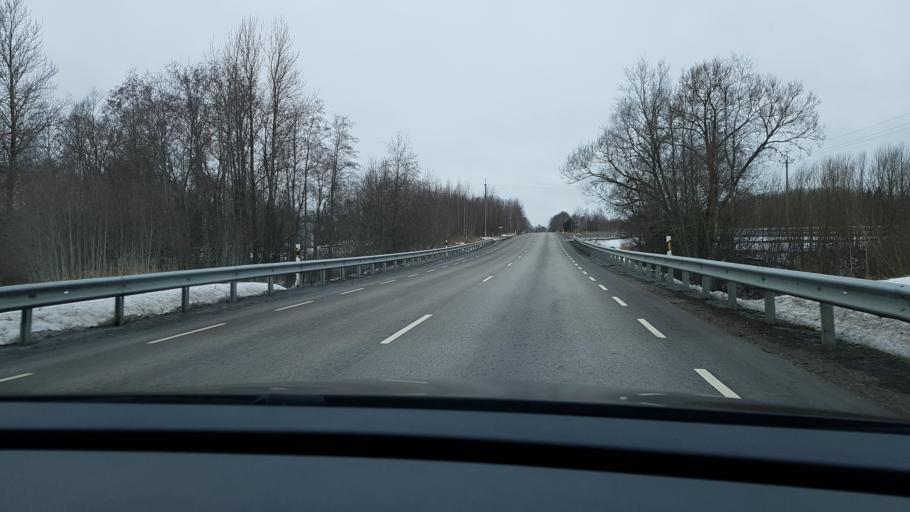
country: EE
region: Paernumaa
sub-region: Sauga vald
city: Sauga
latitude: 58.4423
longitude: 24.4667
